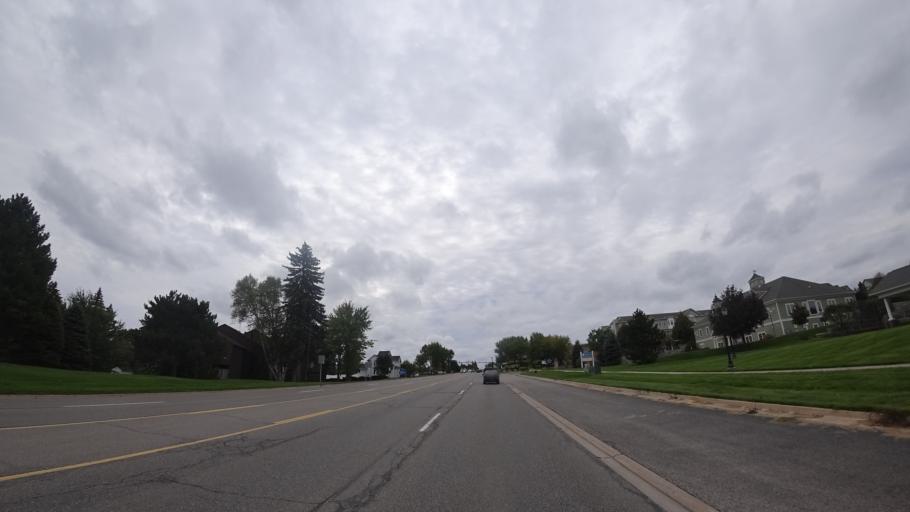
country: US
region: Michigan
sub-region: Emmet County
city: Petoskey
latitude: 45.3651
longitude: -84.9710
